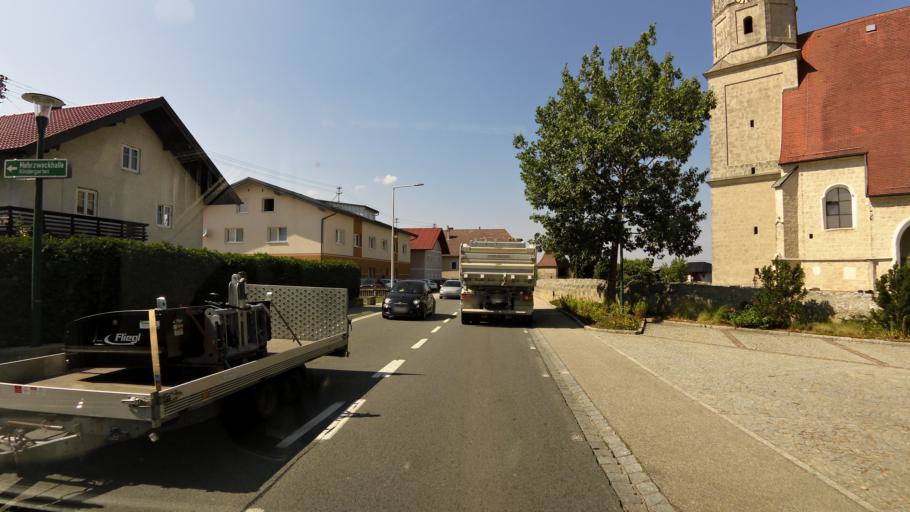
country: AT
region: Upper Austria
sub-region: Politischer Bezirk Braunau am Inn
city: Braunau am Inn
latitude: 48.2034
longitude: 13.1005
